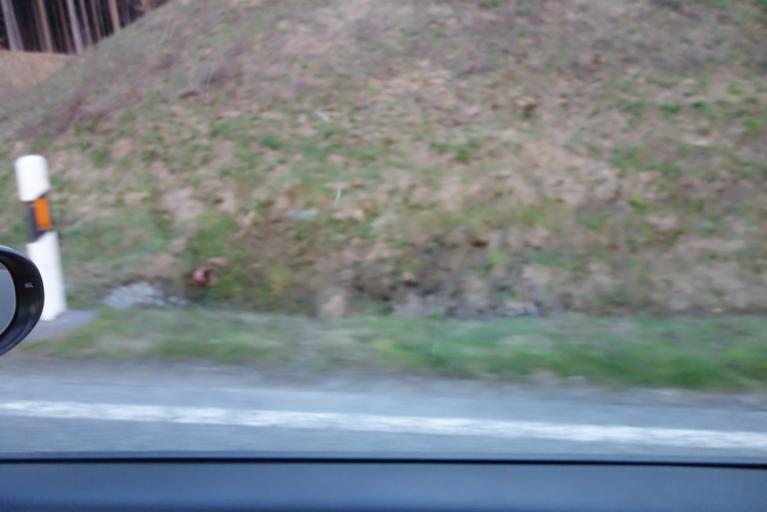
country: DE
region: Saxony
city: Marienberg
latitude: 50.6321
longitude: 13.1597
